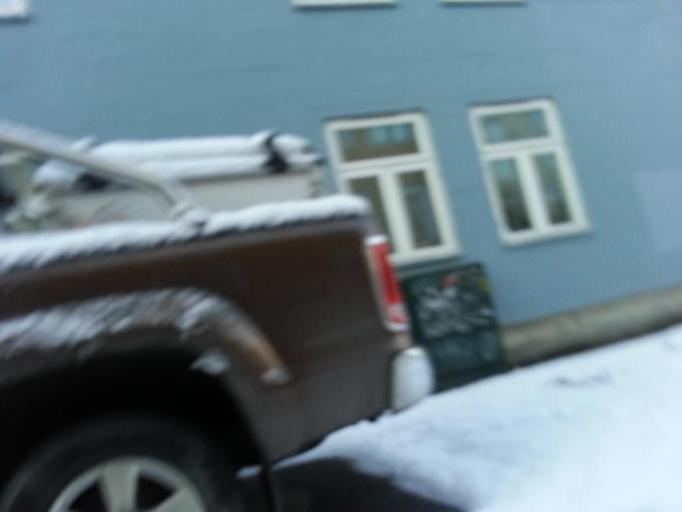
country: NO
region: Sor-Trondelag
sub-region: Trondheim
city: Trondheim
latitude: 63.4302
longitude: 10.4058
